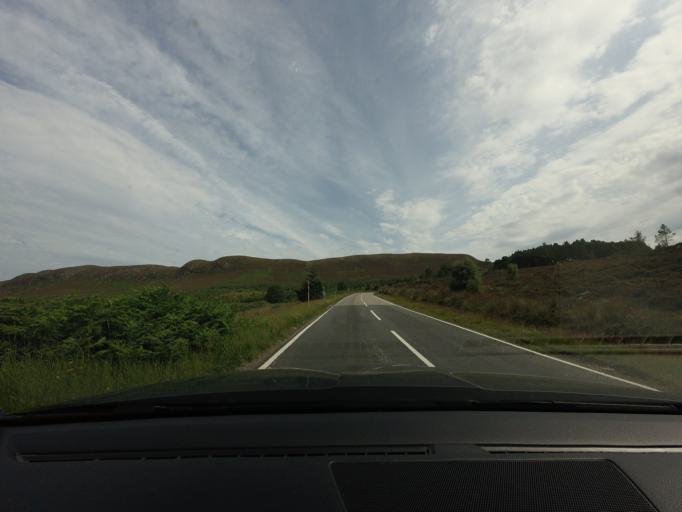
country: GB
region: Scotland
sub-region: Highland
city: Alness
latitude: 57.8408
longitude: -4.2707
